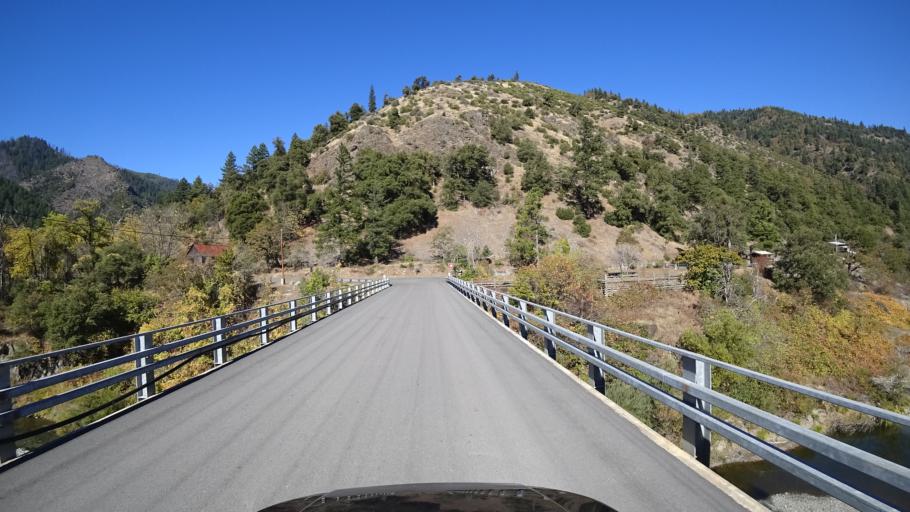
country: US
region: California
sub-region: Humboldt County
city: Willow Creek
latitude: 41.2577
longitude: -123.3221
